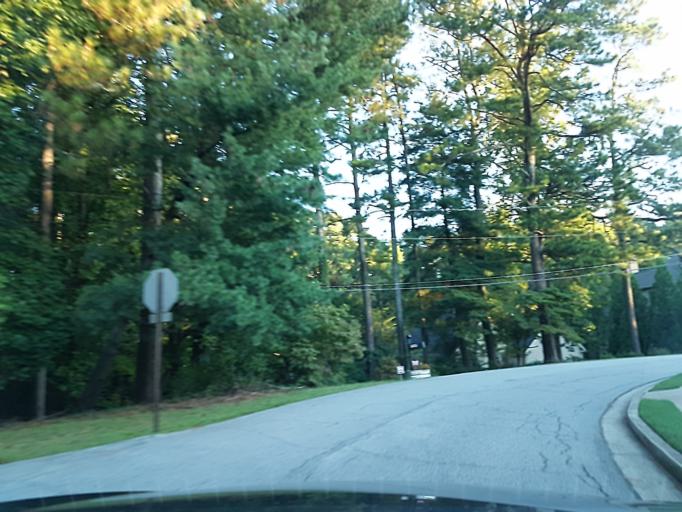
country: US
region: Georgia
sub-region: Cobb County
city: Smyrna
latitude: 33.8611
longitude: -84.4958
